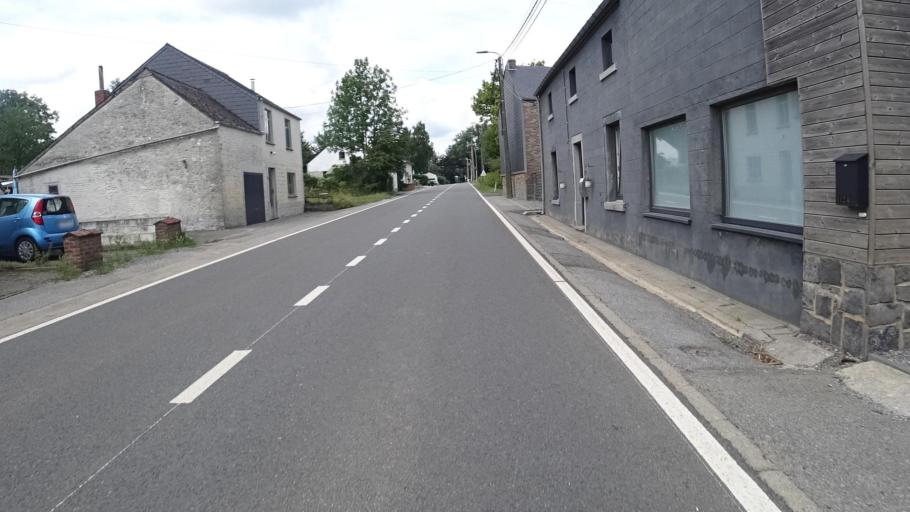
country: BE
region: Wallonia
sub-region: Province de Namur
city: Namur
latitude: 50.5414
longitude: 4.8411
